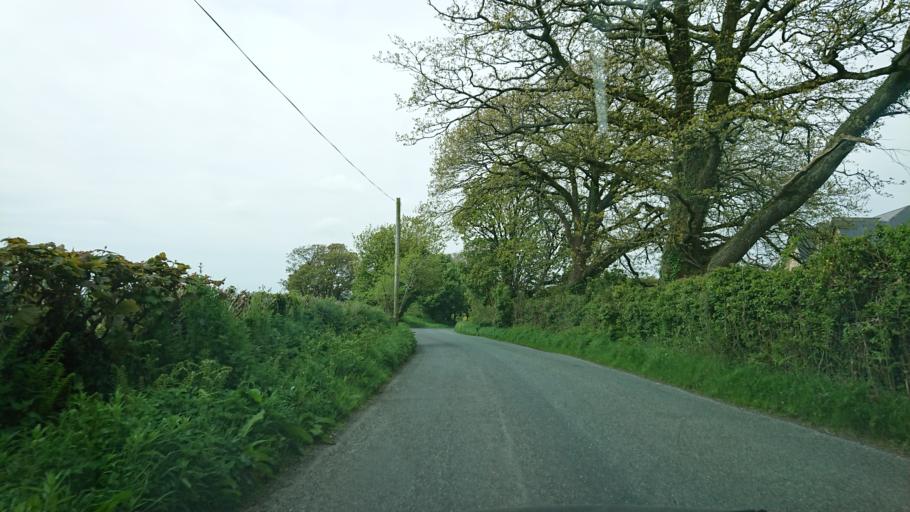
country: IE
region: Munster
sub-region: Waterford
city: Waterford
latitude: 52.2066
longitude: -7.1060
